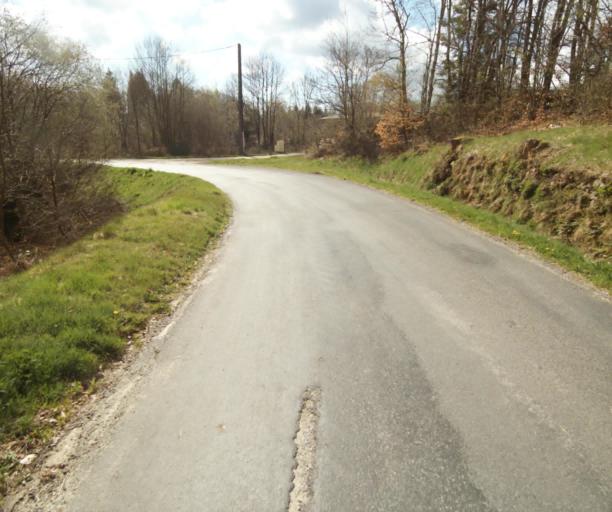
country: FR
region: Limousin
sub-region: Departement de la Correze
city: Correze
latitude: 45.2466
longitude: 1.9478
